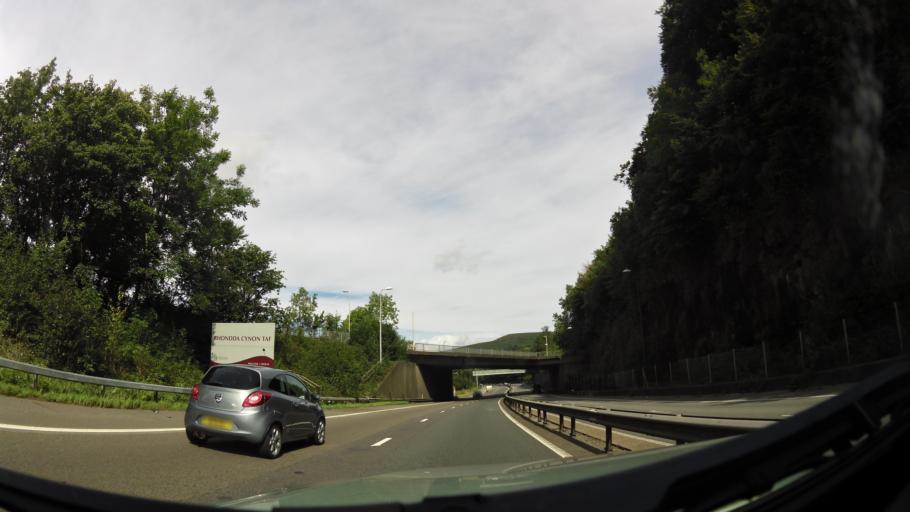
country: GB
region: Wales
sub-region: Cardiff
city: Radyr
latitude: 51.5389
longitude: -3.2611
